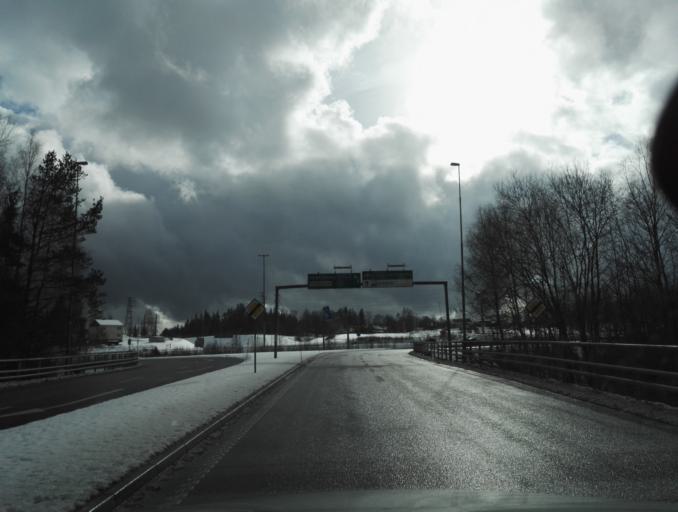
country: SE
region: Vaestra Goetaland
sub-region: Boras Kommun
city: Sjomarken
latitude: 57.7127
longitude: 12.8692
